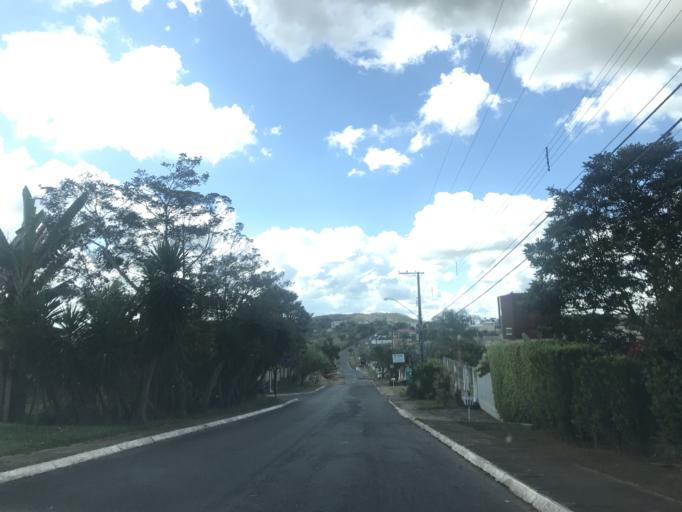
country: BR
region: Federal District
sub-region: Brasilia
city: Brasilia
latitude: -15.8671
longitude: -47.7532
